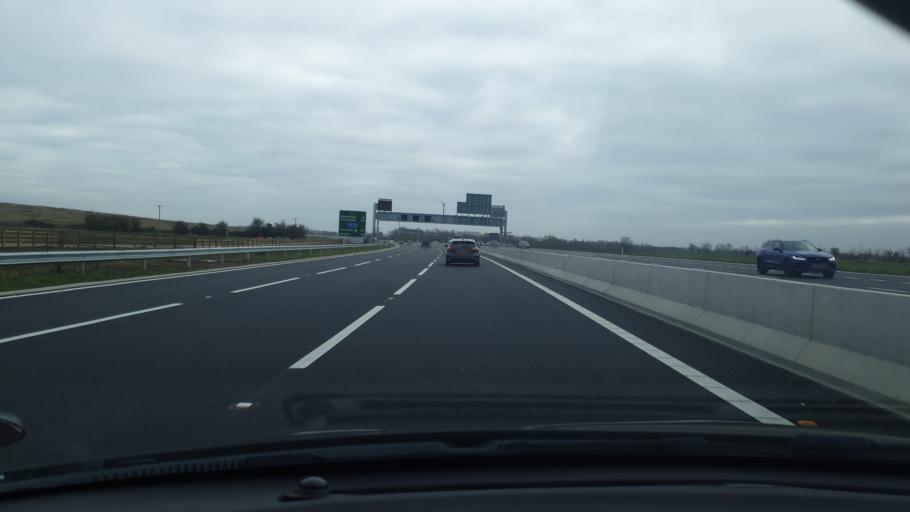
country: GB
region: England
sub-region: Cambridgeshire
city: Buckden
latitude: 52.3027
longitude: -0.2315
